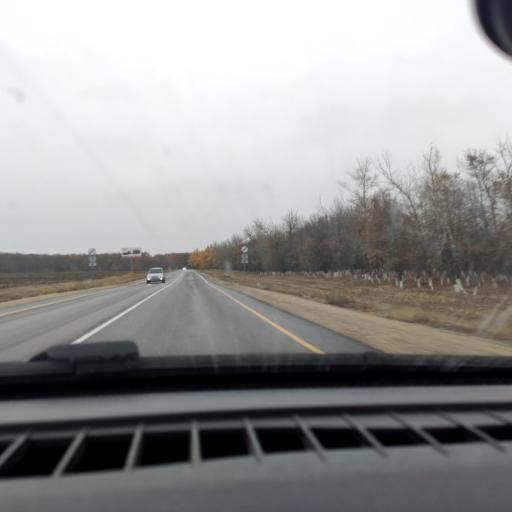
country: RU
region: Voronezj
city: Ostrogozhsk
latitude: 50.9125
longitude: 39.0652
